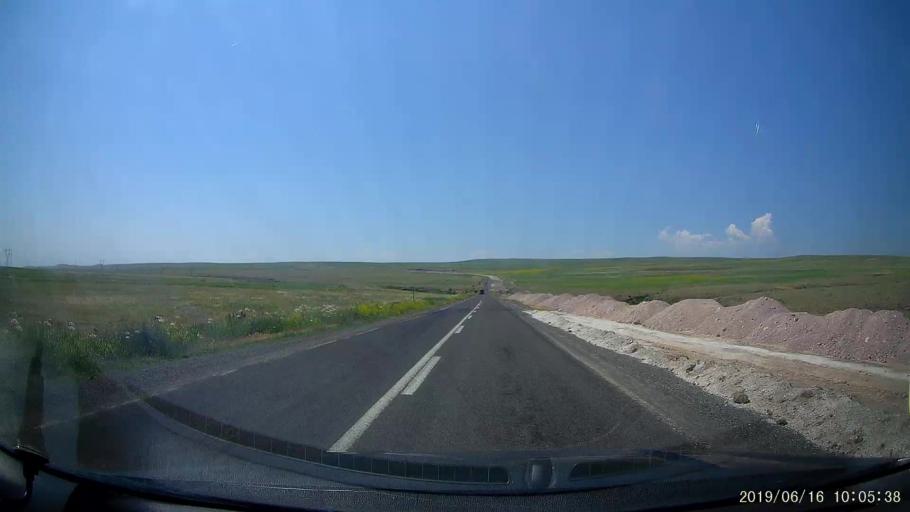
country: TR
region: Kars
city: Digor
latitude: 40.2672
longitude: 43.5392
